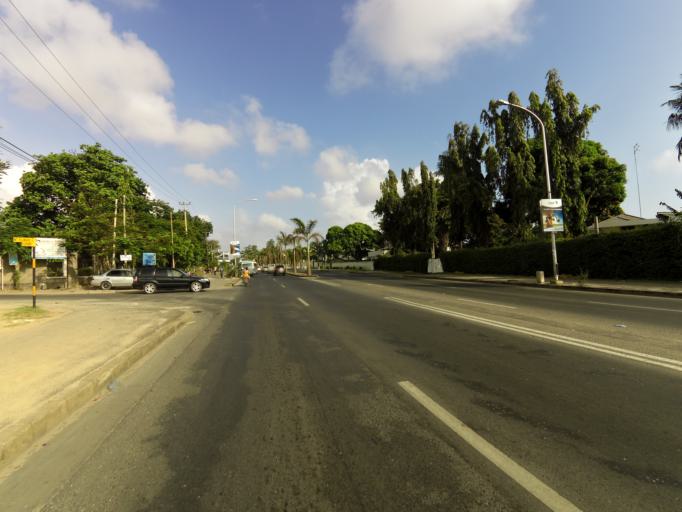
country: TZ
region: Dar es Salaam
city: Magomeni
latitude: -6.7886
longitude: 39.2787
